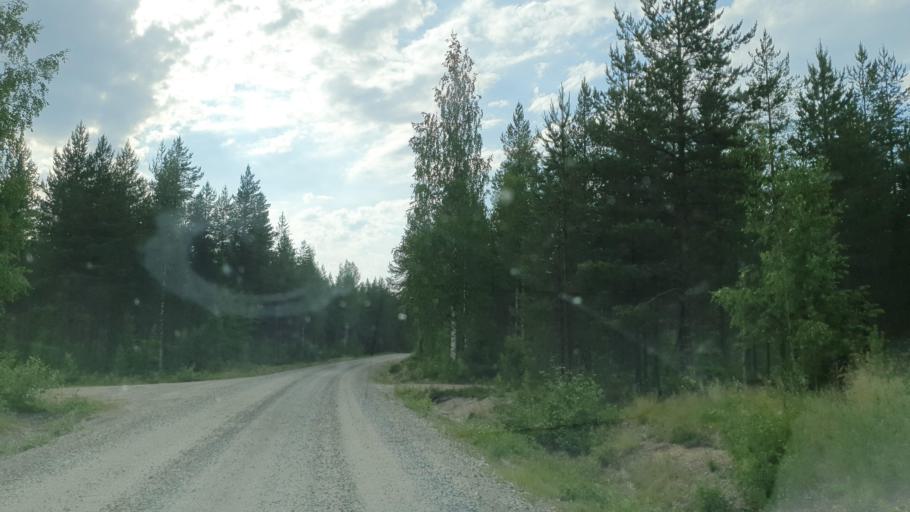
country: FI
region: Kainuu
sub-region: Kehys-Kainuu
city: Kuhmo
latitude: 64.0828
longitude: 29.6910
